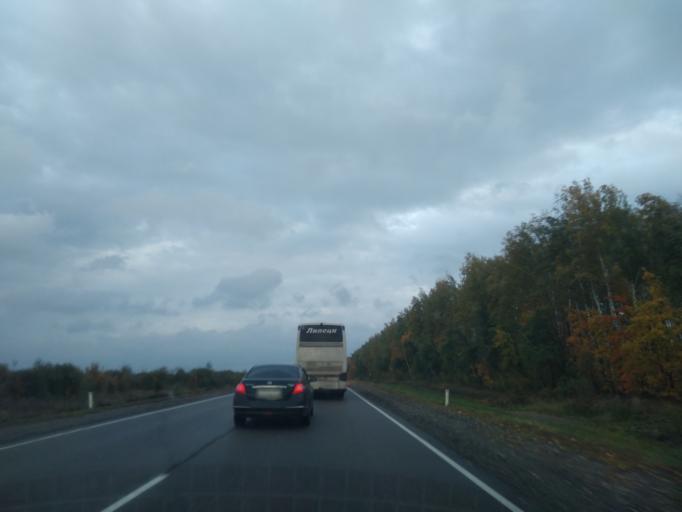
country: RU
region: Lipetsk
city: Borinskoye
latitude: 52.5729
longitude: 39.1922
